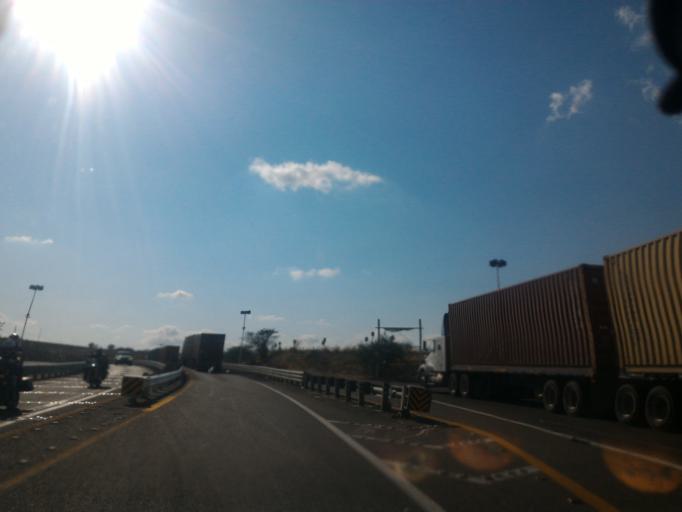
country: MX
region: Jalisco
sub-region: Tonila
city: San Marcos
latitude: 19.4339
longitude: -103.4940
